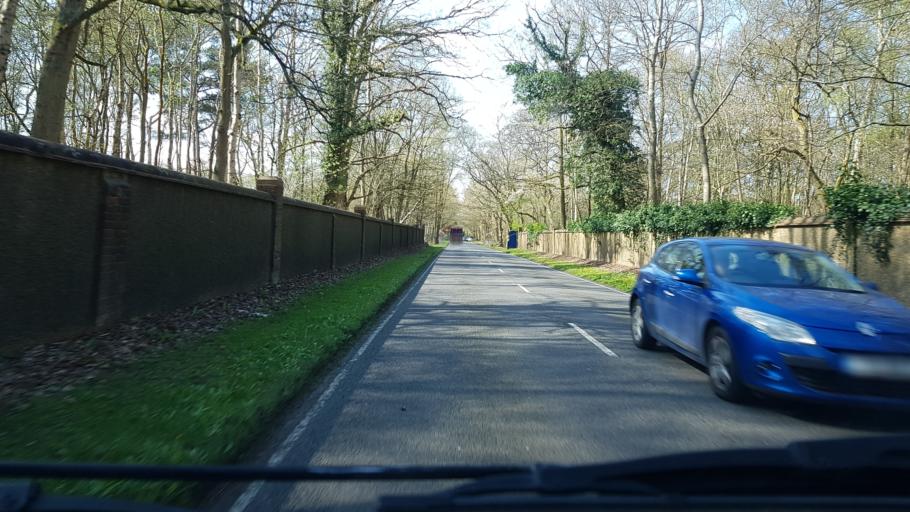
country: GB
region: England
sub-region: Surrey
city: Pirbright
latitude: 51.2977
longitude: -0.6362
